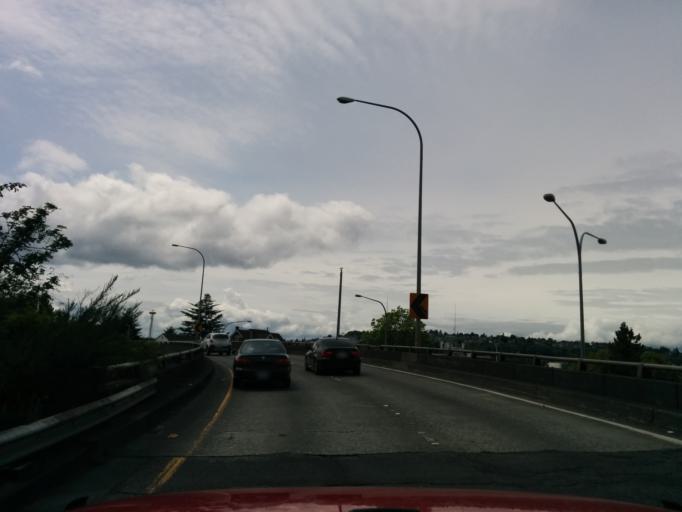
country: US
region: Washington
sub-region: King County
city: Seattle
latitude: 47.6423
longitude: -122.3222
